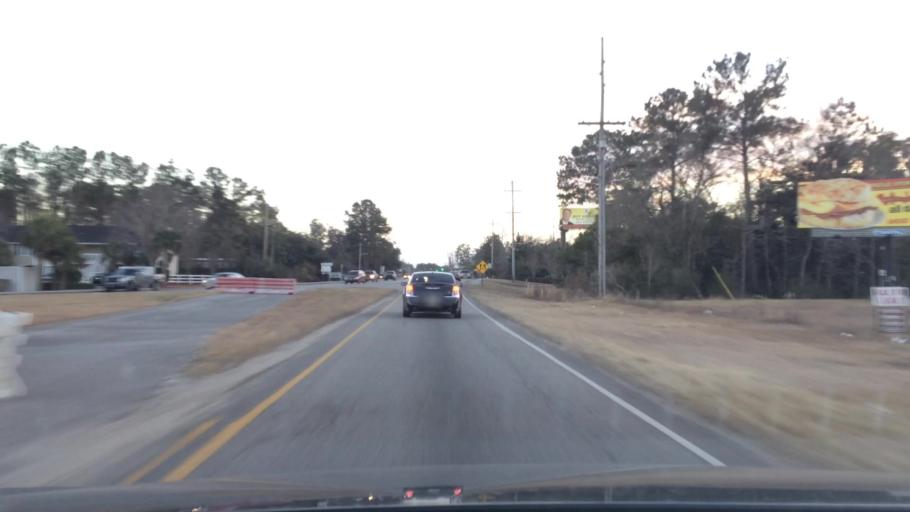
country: US
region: South Carolina
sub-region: Horry County
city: Red Hill
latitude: 33.8029
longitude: -79.0186
